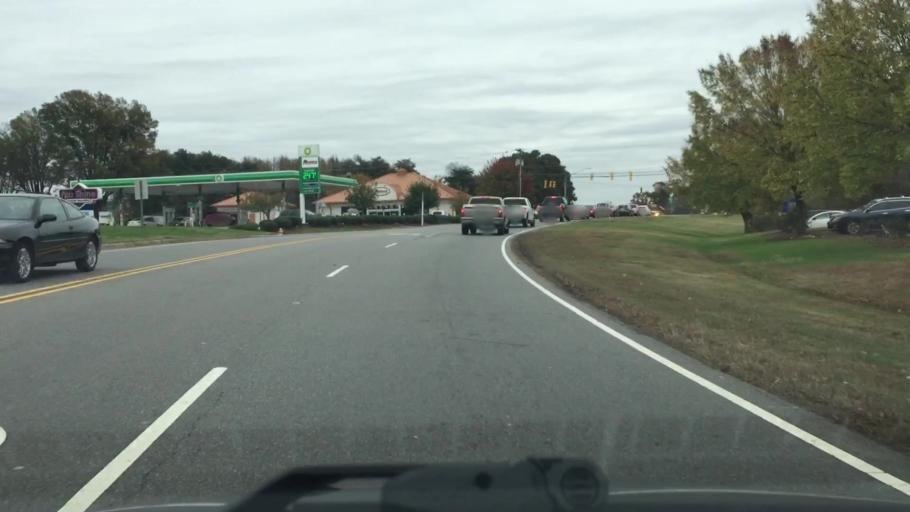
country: US
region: North Carolina
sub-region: Iredell County
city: Mooresville
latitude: 35.5790
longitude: -80.8420
